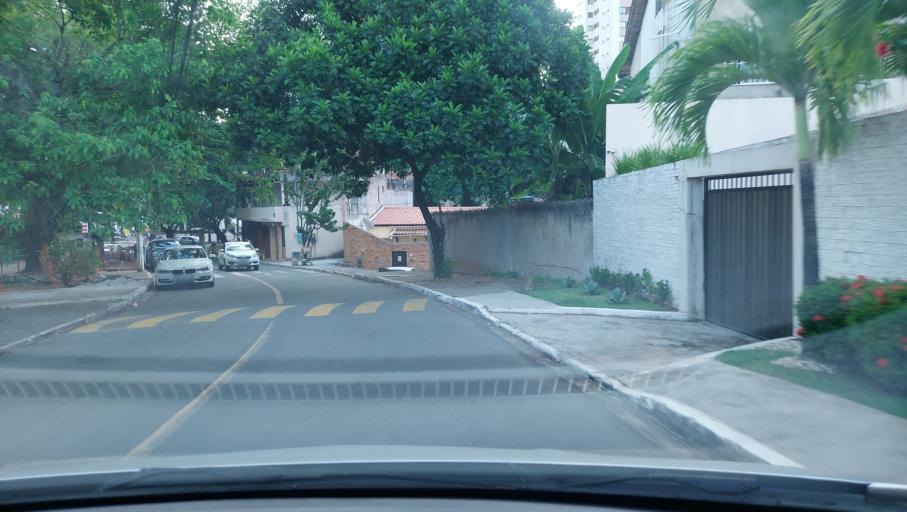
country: BR
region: Bahia
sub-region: Salvador
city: Salvador
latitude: -12.9867
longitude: -38.4475
